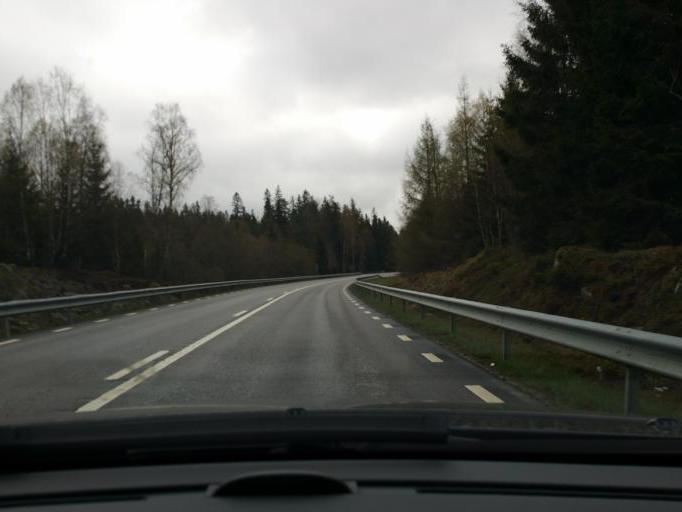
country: SE
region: Kronoberg
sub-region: Vaxjo Kommun
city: Lammhult
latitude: 57.1288
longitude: 14.6247
